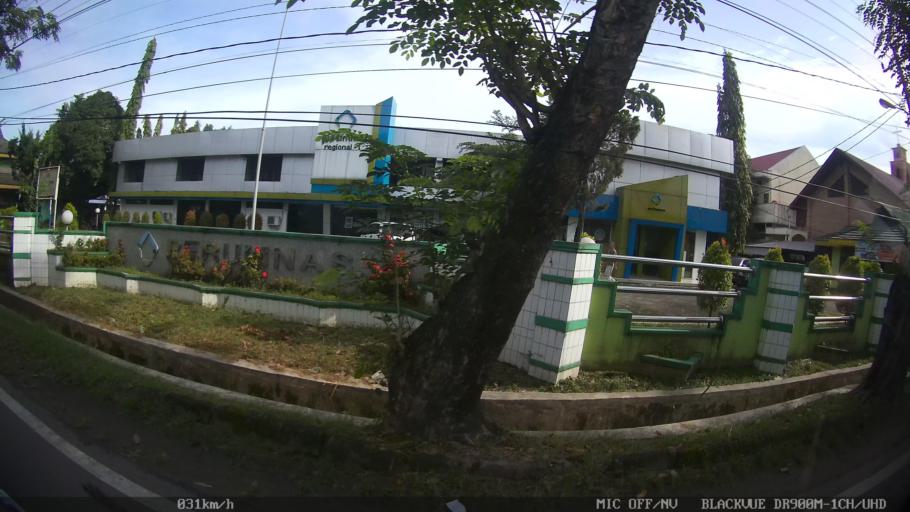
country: ID
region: North Sumatra
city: Sunggal
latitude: 3.6105
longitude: 98.6325
